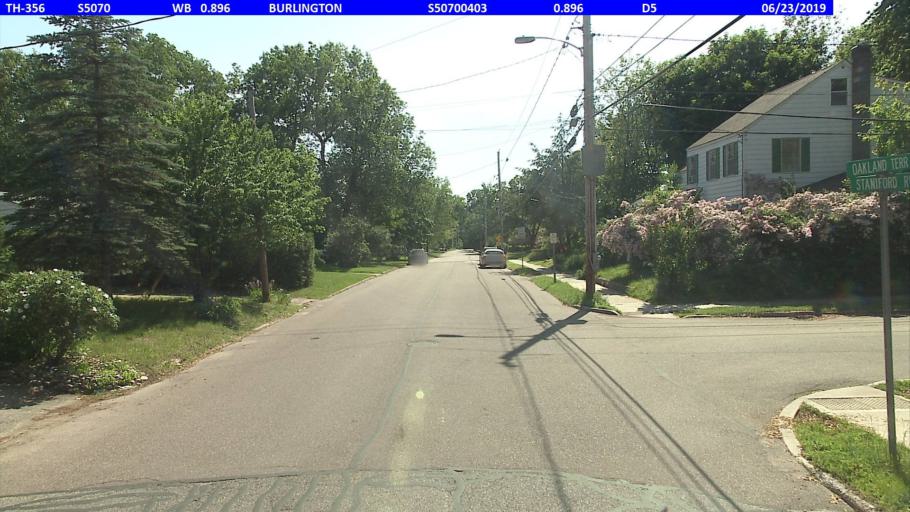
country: US
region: Vermont
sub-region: Chittenden County
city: Burlington
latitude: 44.5094
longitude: -73.2578
